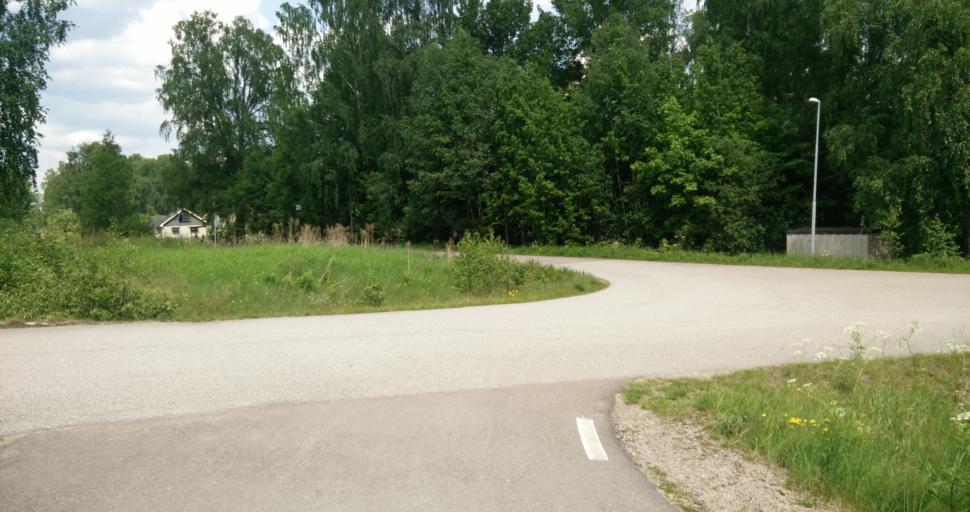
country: SE
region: Vaermland
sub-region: Hagfors Kommun
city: Hagfors
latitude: 60.0066
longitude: 13.6034
